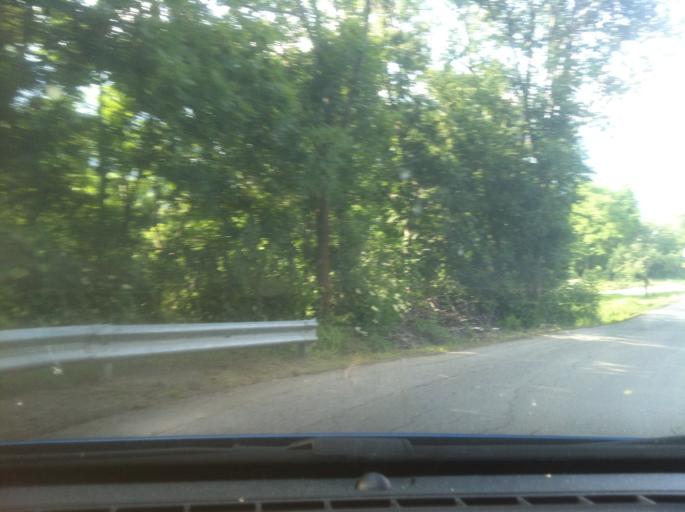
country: IT
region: Aosta Valley
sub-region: Valle d'Aosta
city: Saint Marcel
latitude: 45.7235
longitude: 7.4554
